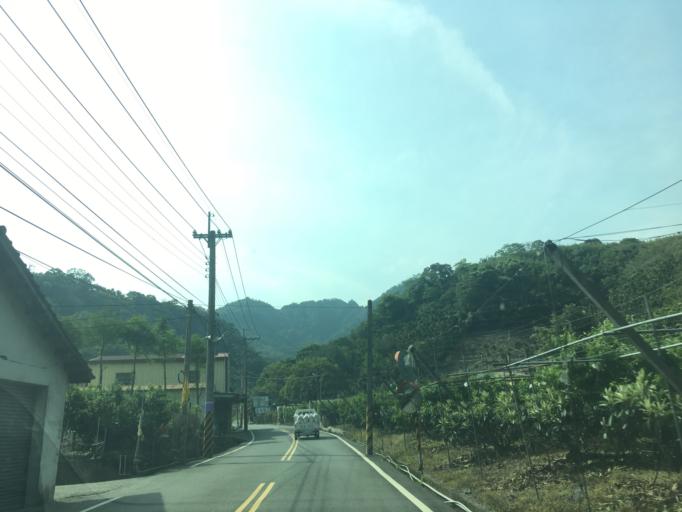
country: TW
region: Taiwan
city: Fengyuan
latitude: 24.1649
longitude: 120.8249
